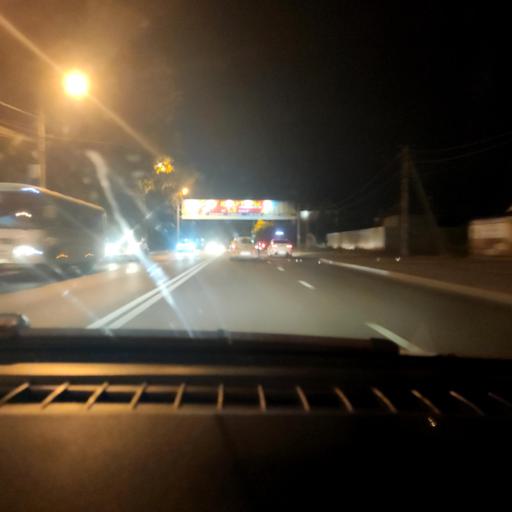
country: RU
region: Voronezj
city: Voronezh
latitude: 51.6977
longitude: 39.1966
